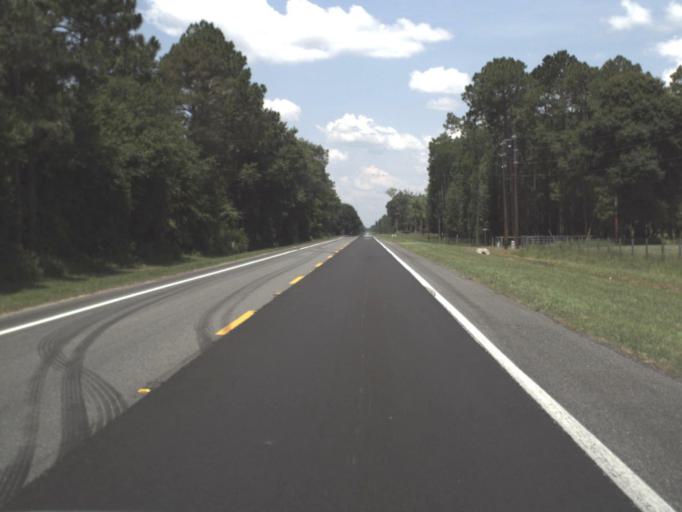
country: US
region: Florida
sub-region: Union County
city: Lake Butler
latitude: 30.0355
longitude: -82.3737
